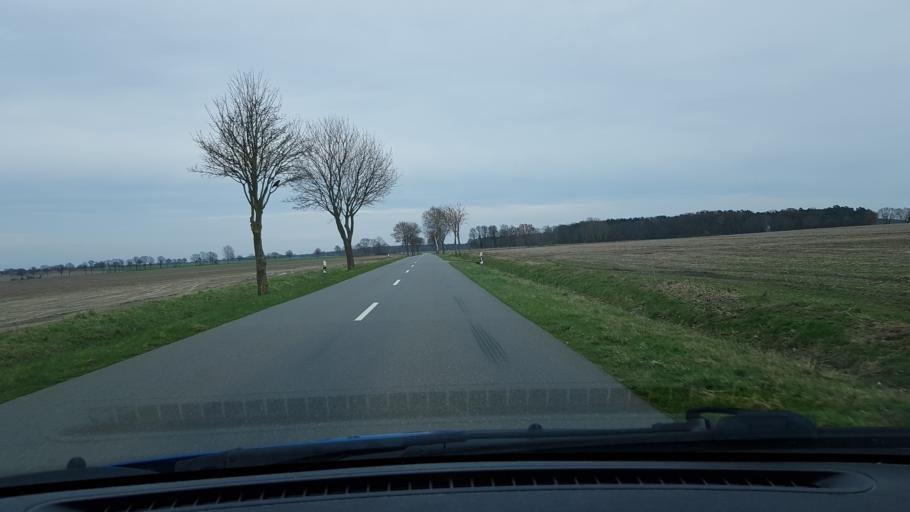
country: DE
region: Lower Saxony
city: Emmendorf
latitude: 53.0022
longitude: 10.6176
